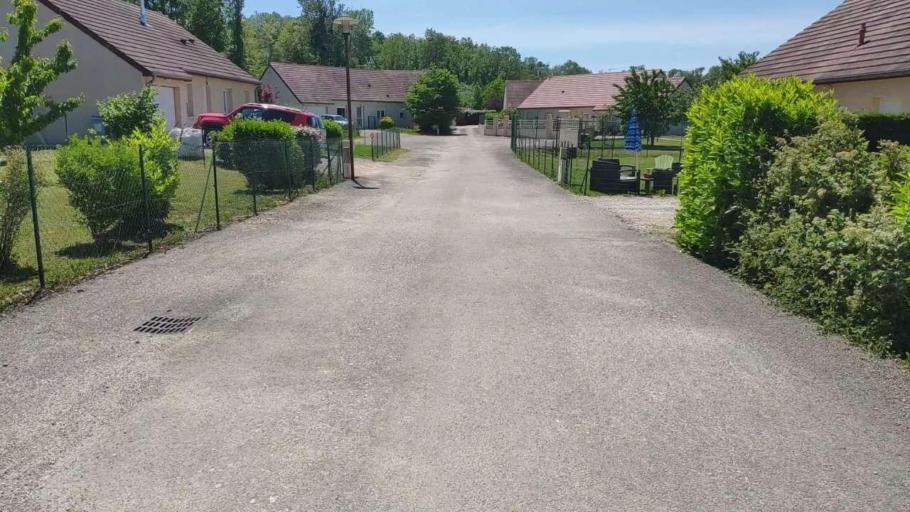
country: FR
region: Franche-Comte
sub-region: Departement du Jura
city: Bletterans
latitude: 46.7424
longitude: 5.4374
